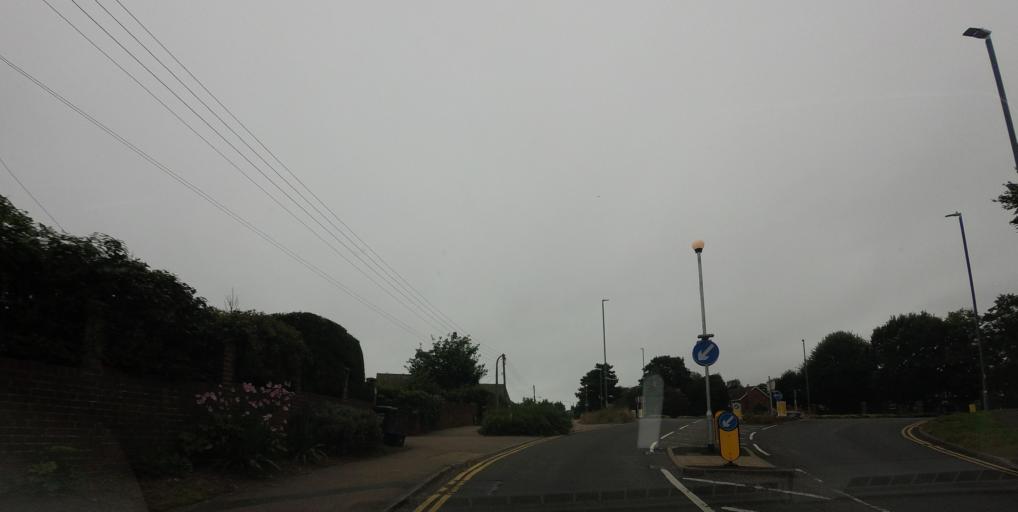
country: GB
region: England
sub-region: Kent
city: Stone
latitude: 51.4339
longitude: 0.2505
